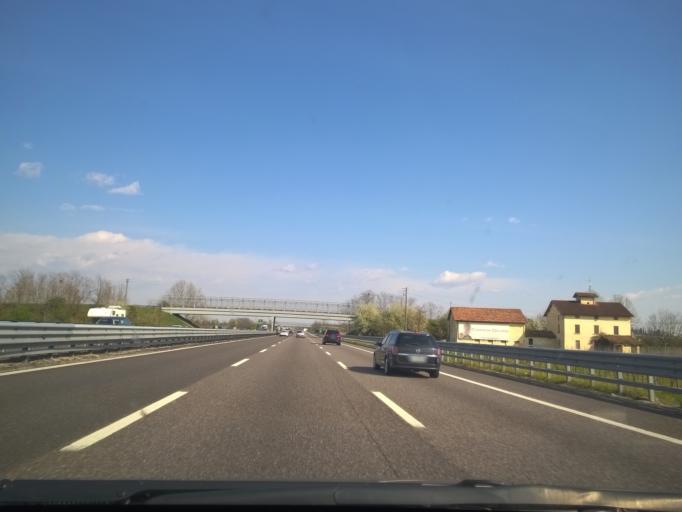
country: IT
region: Lombardy
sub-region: Provincia di Brescia
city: San Martino della Battaglia
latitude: 45.4374
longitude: 10.5828
